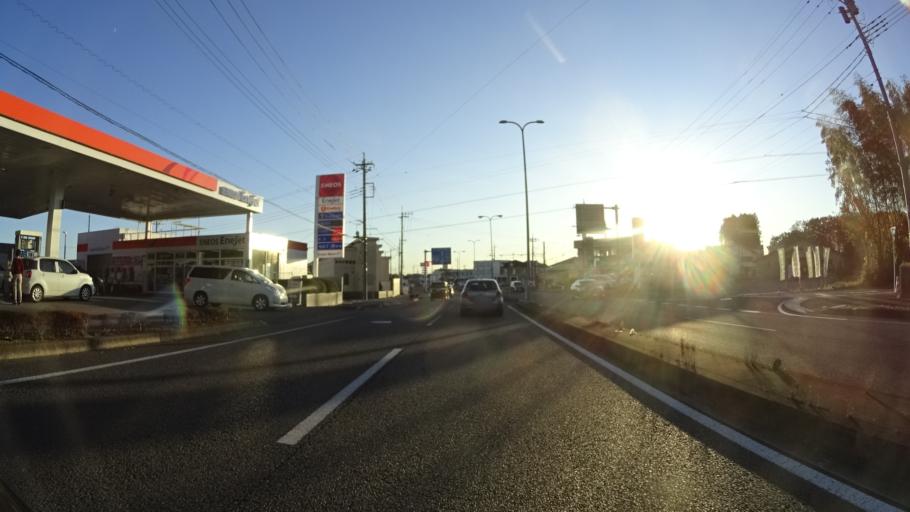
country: JP
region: Tochigi
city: Utsunomiya-shi
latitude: 36.5529
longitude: 139.8506
